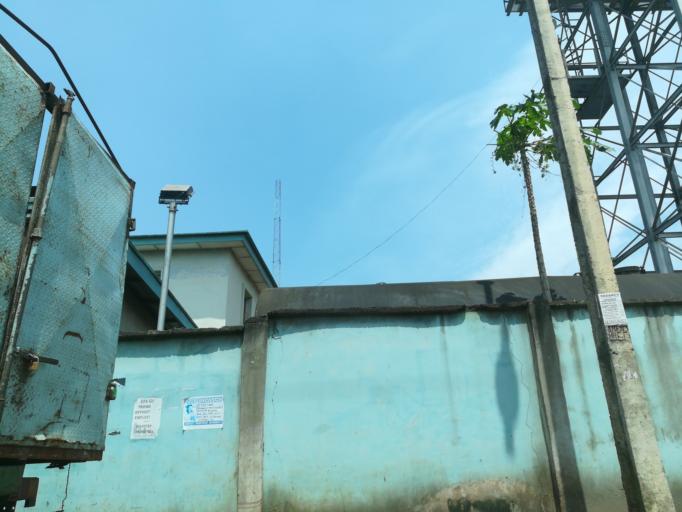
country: NG
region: Lagos
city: Ikorodu
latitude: 6.6230
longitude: 3.4965
